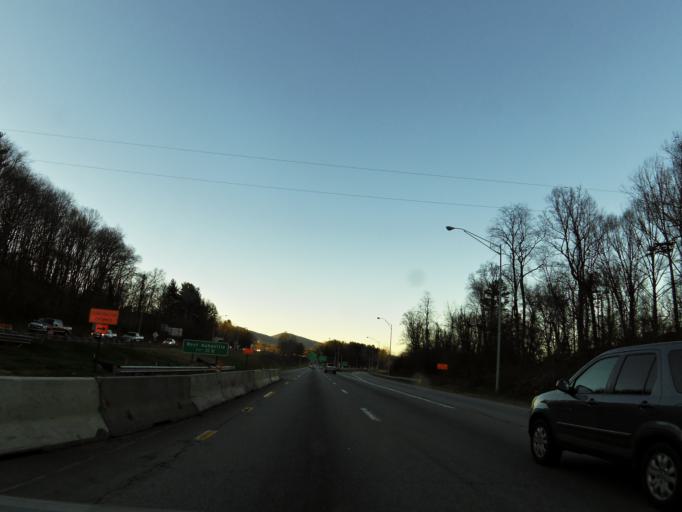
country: US
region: North Carolina
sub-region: Buncombe County
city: Bent Creek
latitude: 35.5477
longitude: -82.6061
